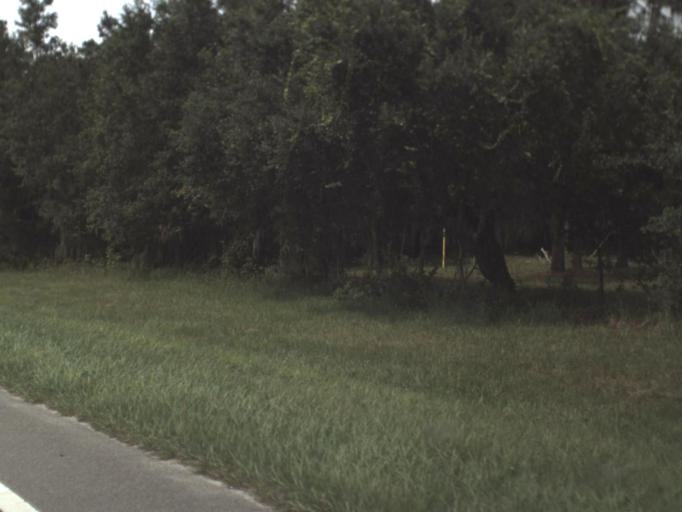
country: US
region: Florida
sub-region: Hillsborough County
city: Wimauma
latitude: 27.5803
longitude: -82.1979
